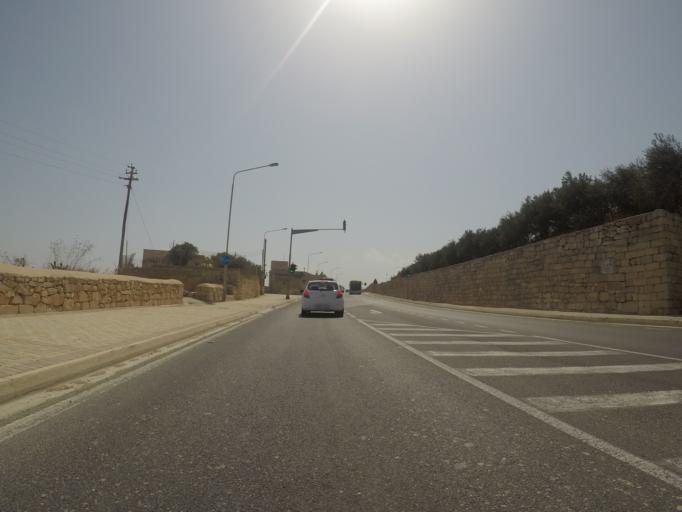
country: MT
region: L-Imtarfa
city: Imtarfa
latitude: 35.9124
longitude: 14.3957
